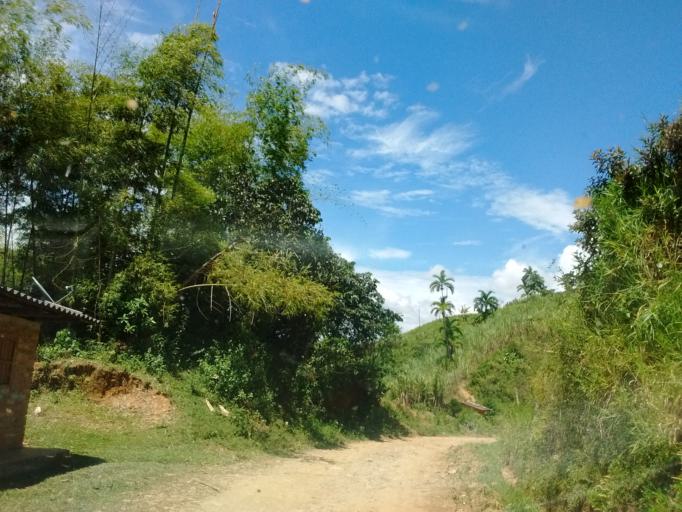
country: CO
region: Cauca
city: Villa Rica
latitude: 2.6330
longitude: -76.7700
